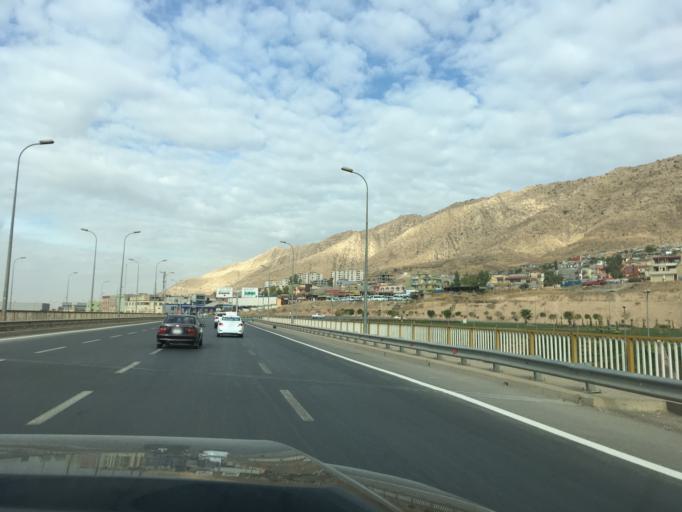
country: IQ
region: Dahuk
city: Sinah
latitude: 36.8507
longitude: 43.0514
